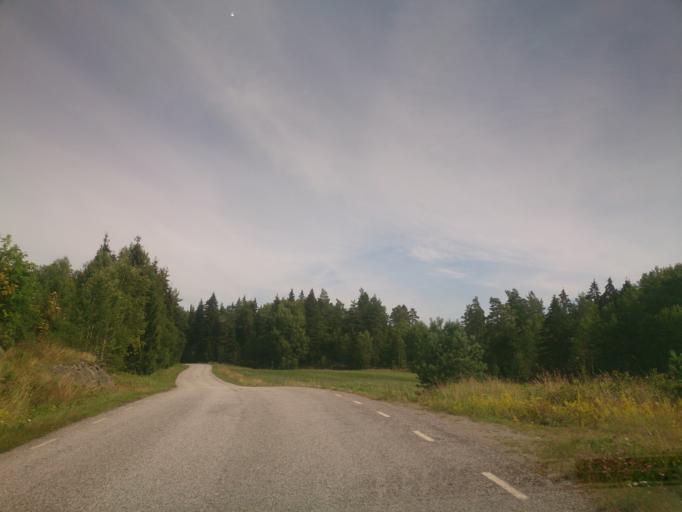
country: SE
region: OEstergoetland
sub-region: Valdemarsviks Kommun
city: Gusum
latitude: 58.3283
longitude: 16.5816
